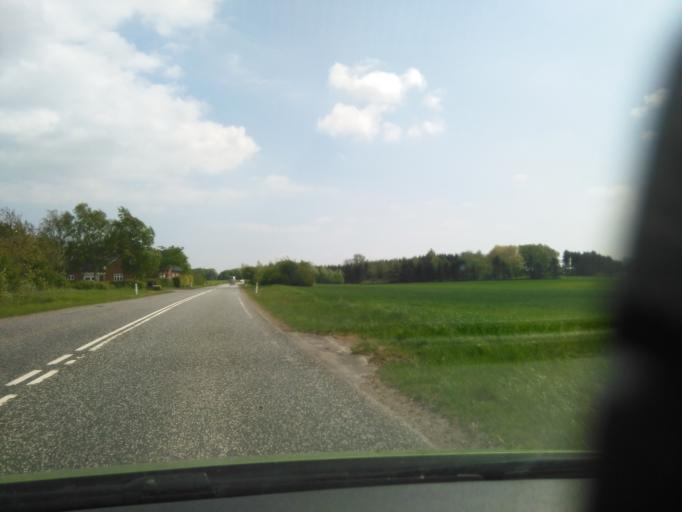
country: DK
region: Central Jutland
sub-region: Arhus Kommune
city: Solbjerg
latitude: 55.9842
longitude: 10.0413
